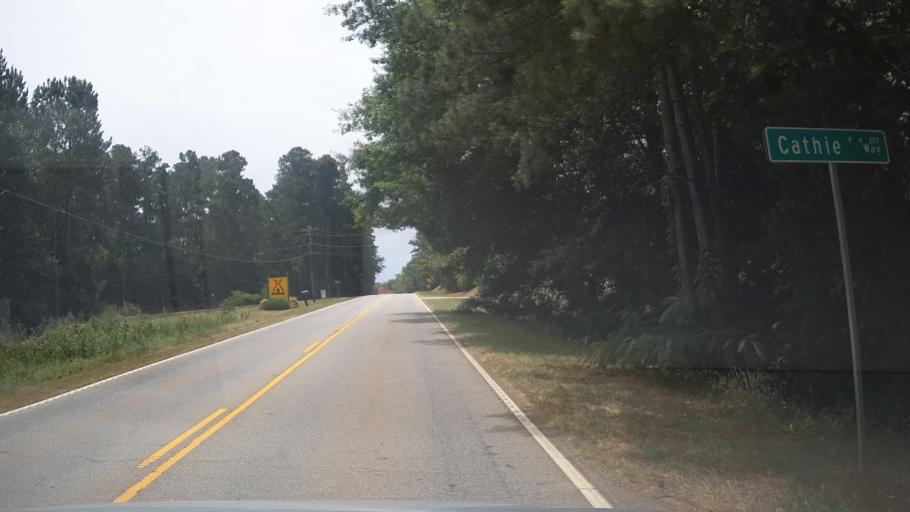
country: US
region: South Carolina
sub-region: Anderson County
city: Centerville
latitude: 34.5357
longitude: -82.8031
